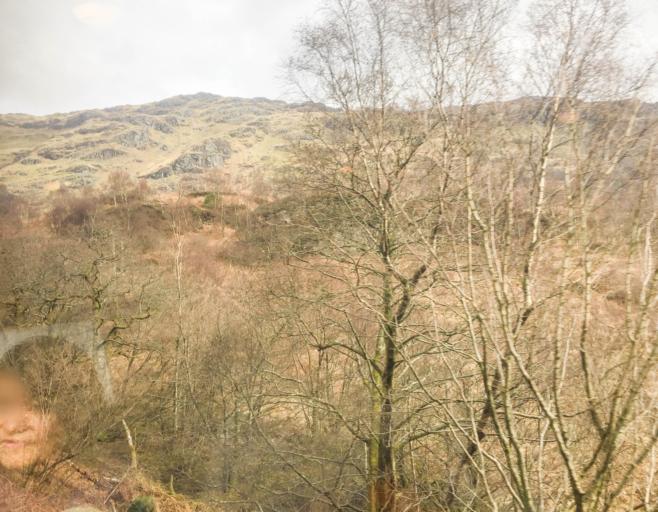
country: GB
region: Scotland
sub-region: Argyll and Bute
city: Garelochhead
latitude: 56.2810
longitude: -4.7047
